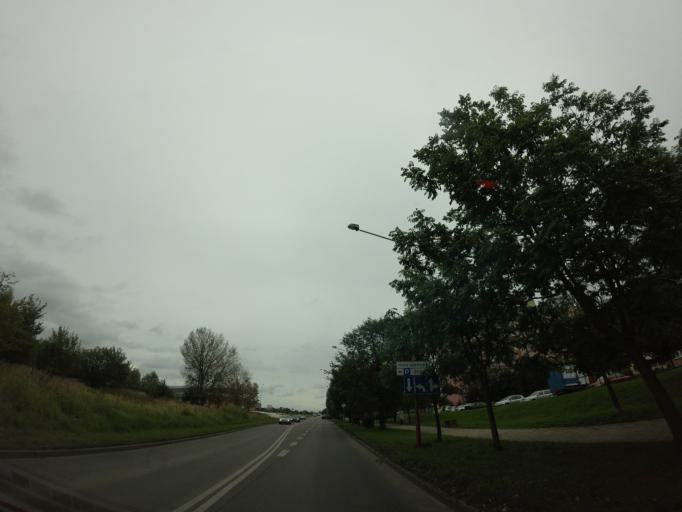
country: PL
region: West Pomeranian Voivodeship
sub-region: Szczecin
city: Szczecin
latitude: 53.4565
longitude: 14.4889
